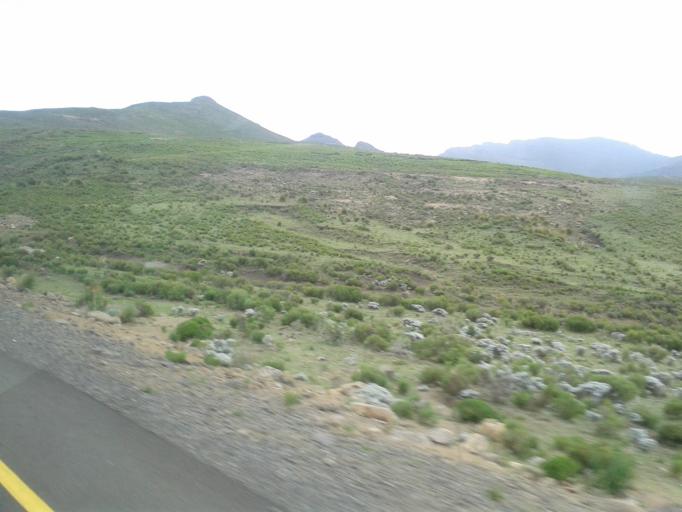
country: LS
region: Maseru
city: Nako
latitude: -29.7544
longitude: 27.9751
